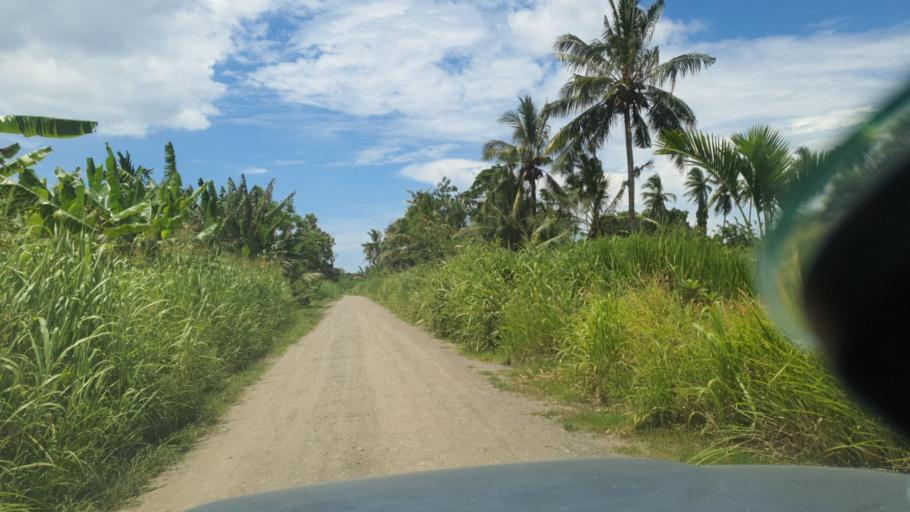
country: SB
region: Guadalcanal
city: Honiara
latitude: -9.4481
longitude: 160.1843
